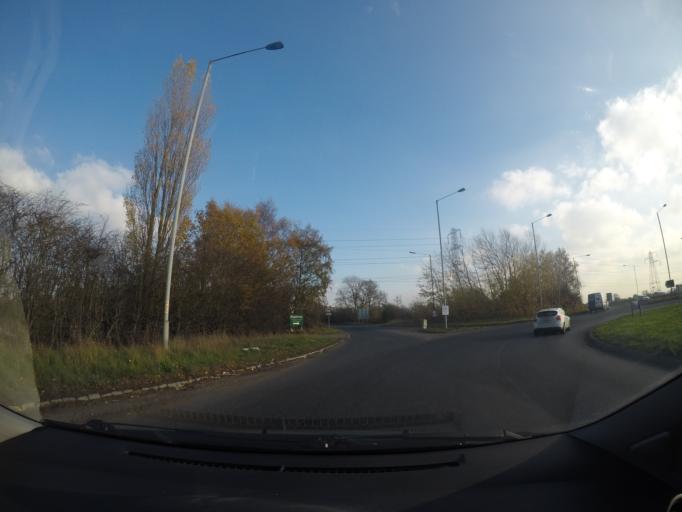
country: GB
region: England
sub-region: City of York
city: Huntington
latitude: 53.9991
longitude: -1.0427
